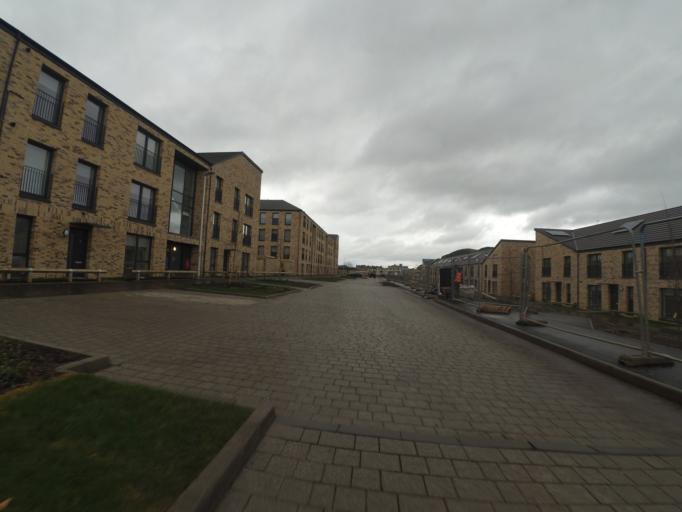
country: GB
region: Scotland
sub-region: West Lothian
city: Seafield
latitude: 55.9340
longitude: -3.1336
